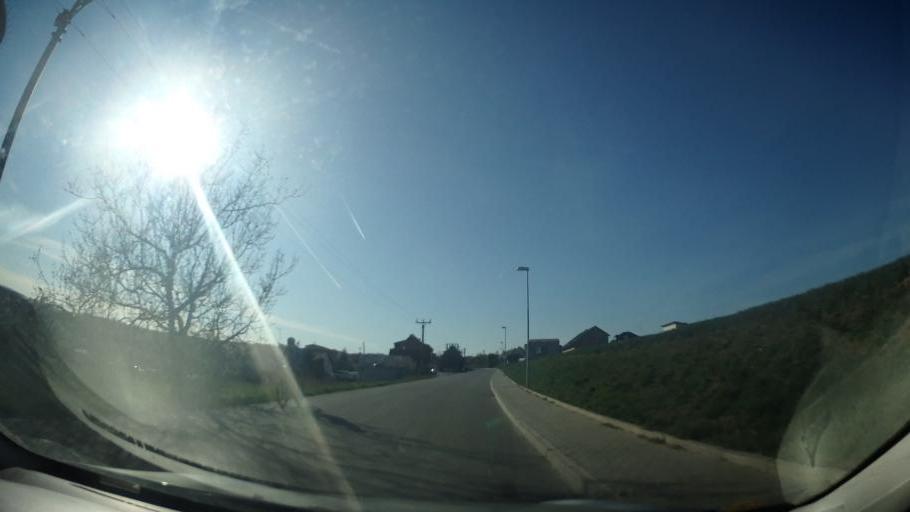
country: CZ
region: South Moravian
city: Moravany
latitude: 49.1459
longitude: 16.5852
